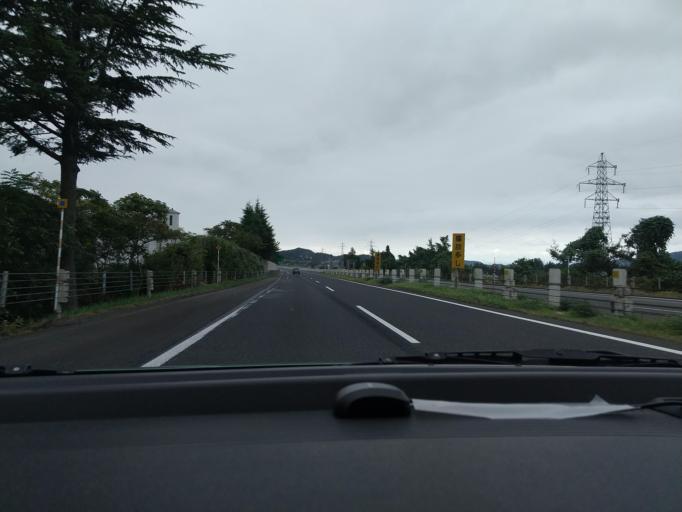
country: JP
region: Iwate
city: Ichinoseki
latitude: 38.9700
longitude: 141.1127
